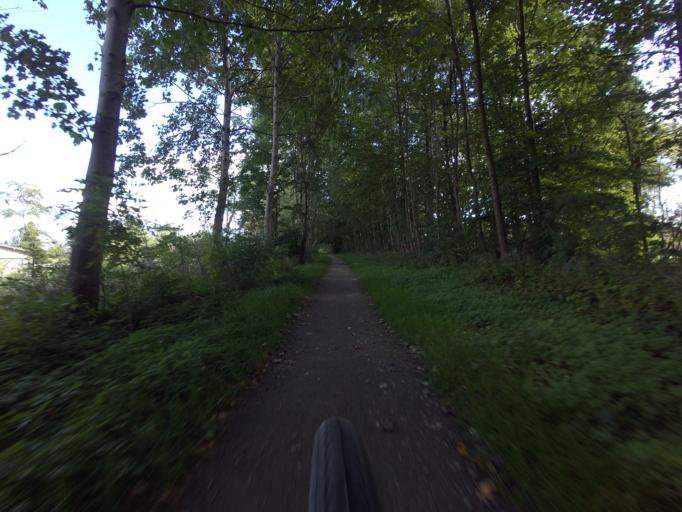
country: DK
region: South Denmark
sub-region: Vejle Kommune
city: Give
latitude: 55.9819
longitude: 9.2935
